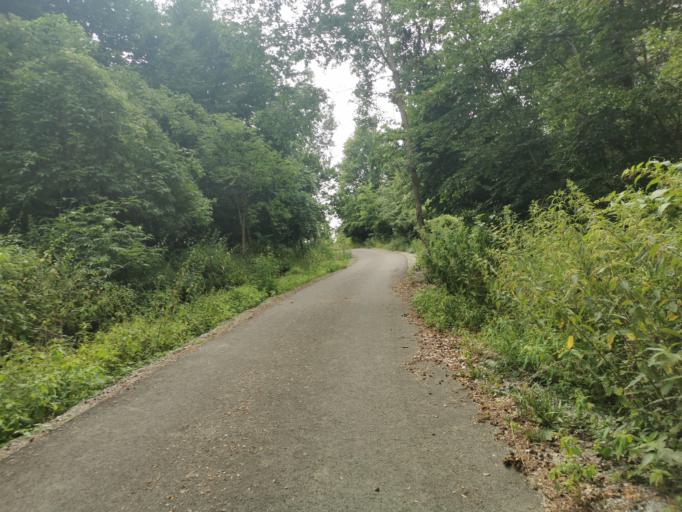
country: SK
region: Nitriansky
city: Brezova pod Bradlom
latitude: 48.7257
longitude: 17.5039
